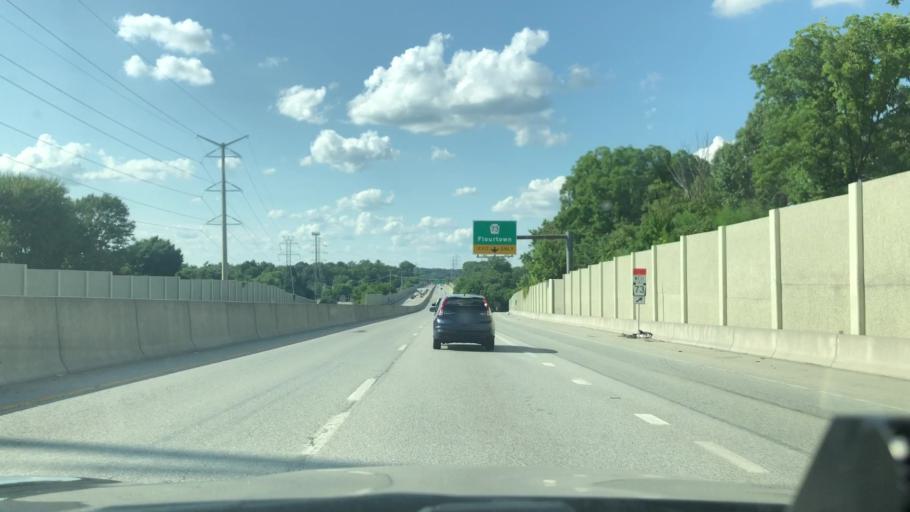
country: US
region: Pennsylvania
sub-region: Montgomery County
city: Flourtown
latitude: 40.1092
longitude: -75.1991
